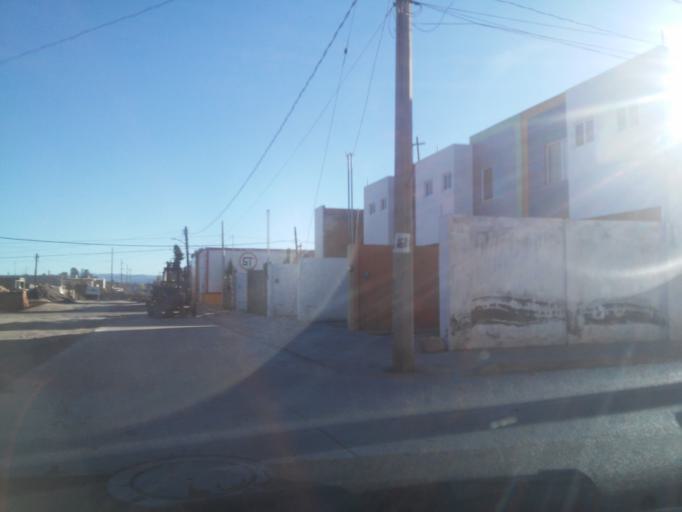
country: MX
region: Durango
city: Victoria de Durango
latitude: 24.0139
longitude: -104.6336
